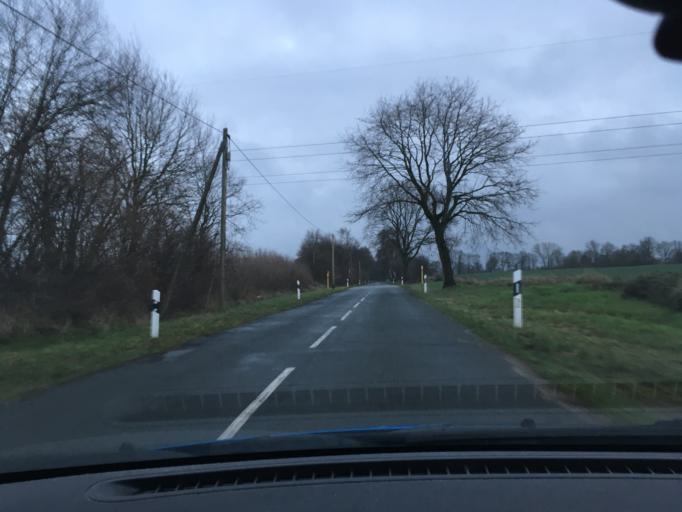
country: DE
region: Mecklenburg-Vorpommern
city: Nostorf
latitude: 53.3975
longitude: 10.6835
